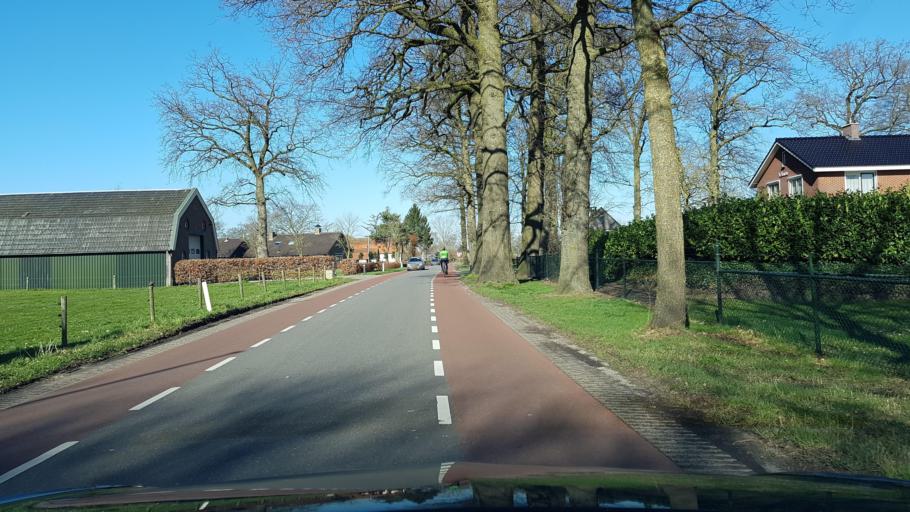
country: NL
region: Gelderland
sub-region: Gemeente Ede
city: Ederveen
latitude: 52.0360
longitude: 5.5992
